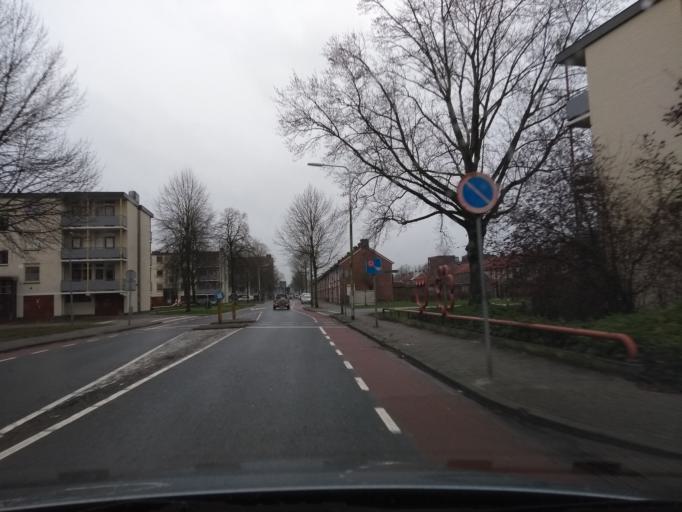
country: NL
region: Overijssel
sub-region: Gemeente Almelo
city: Almelo
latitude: 52.3501
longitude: 6.6451
